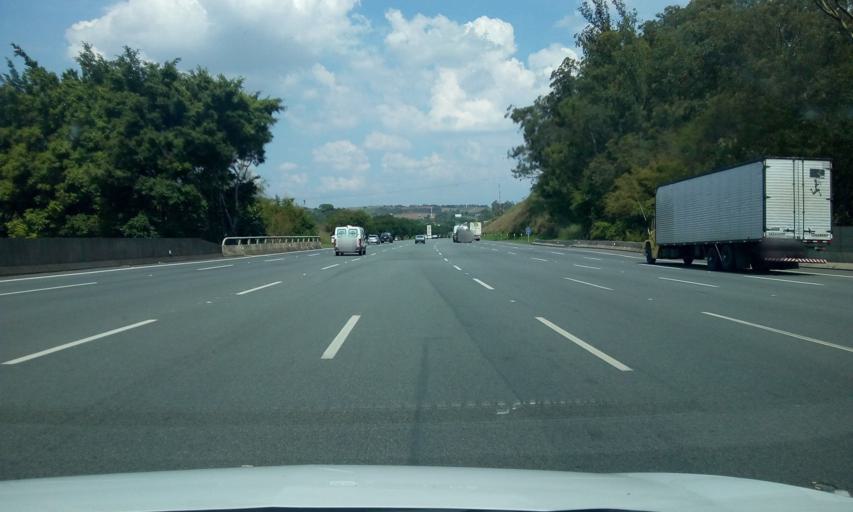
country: BR
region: Sao Paulo
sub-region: Vinhedo
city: Vinhedo
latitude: -23.0599
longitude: -47.0425
